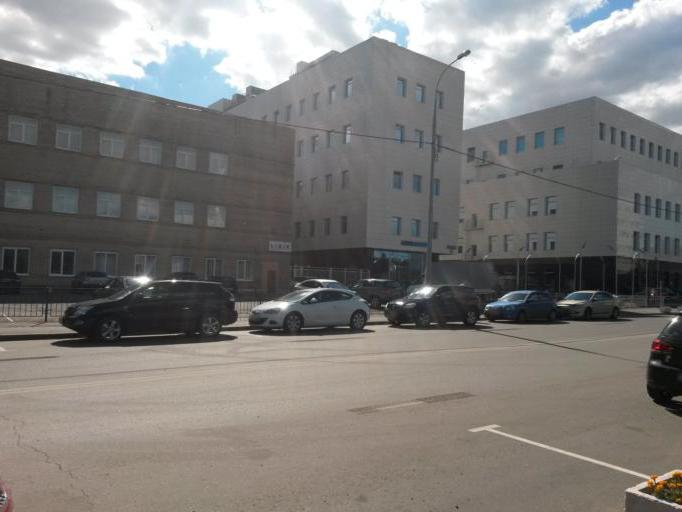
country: RU
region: Moskovskaya
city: Kozhukhovo
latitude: 55.7038
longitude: 37.6944
